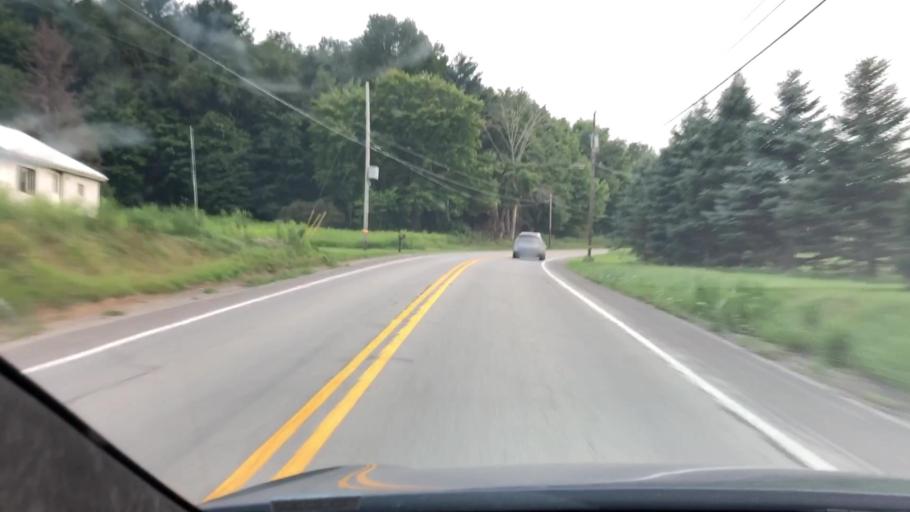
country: US
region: Pennsylvania
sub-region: Mercer County
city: Grove City
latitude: 41.1702
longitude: -79.9894
